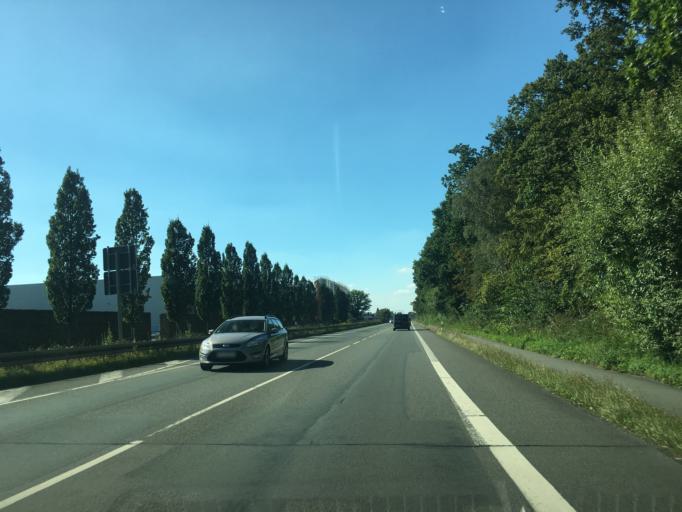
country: DE
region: North Rhine-Westphalia
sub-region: Regierungsbezirk Detmold
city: Rheda-Wiedenbruck
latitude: 51.8747
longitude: 8.2492
